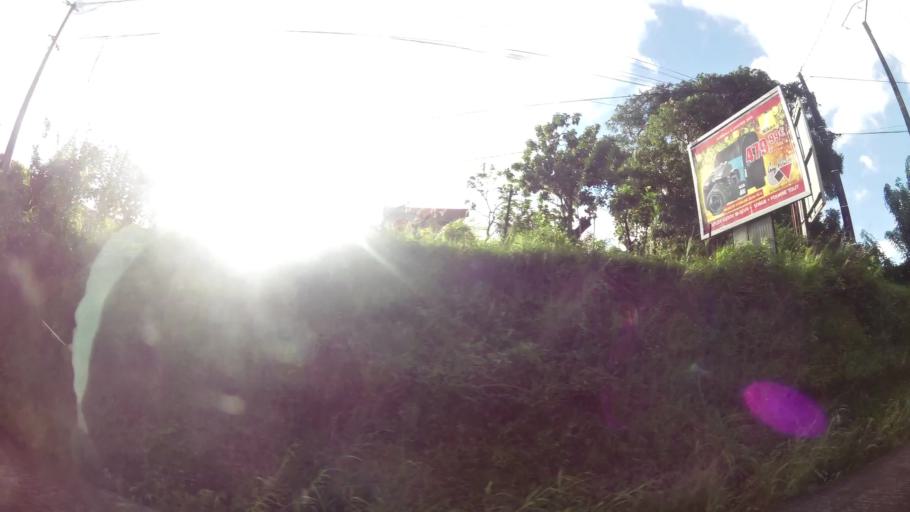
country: MQ
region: Martinique
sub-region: Martinique
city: Le Francois
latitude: 14.6004
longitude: -60.9414
